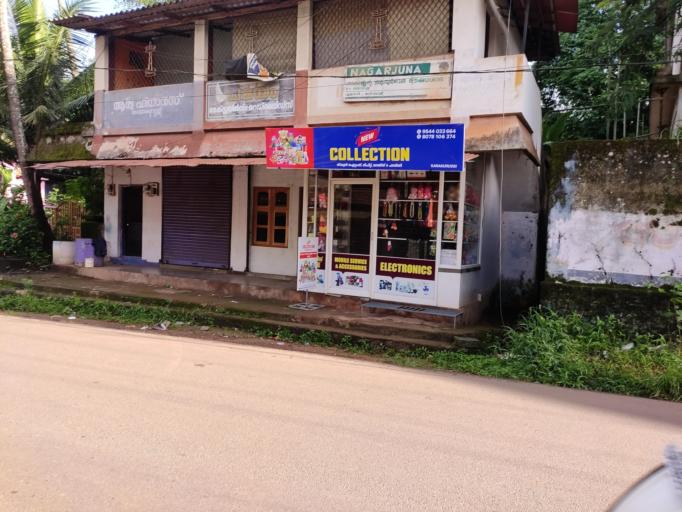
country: IN
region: Kerala
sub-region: Palakkad district
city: Mannarakkat
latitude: 10.9317
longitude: 76.4904
